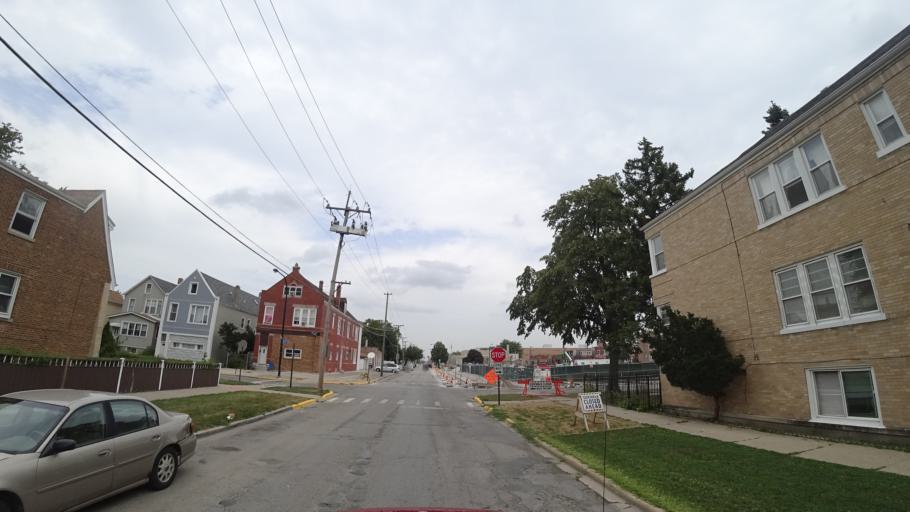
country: US
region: Illinois
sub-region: Cook County
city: Cicero
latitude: 41.8489
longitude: -87.7589
